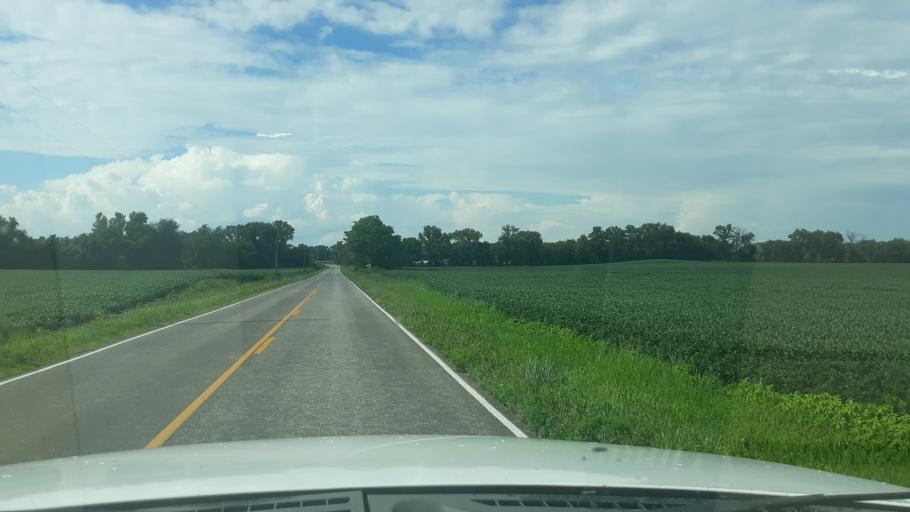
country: US
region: Illinois
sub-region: Saline County
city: Eldorado
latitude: 37.8560
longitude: -88.5304
